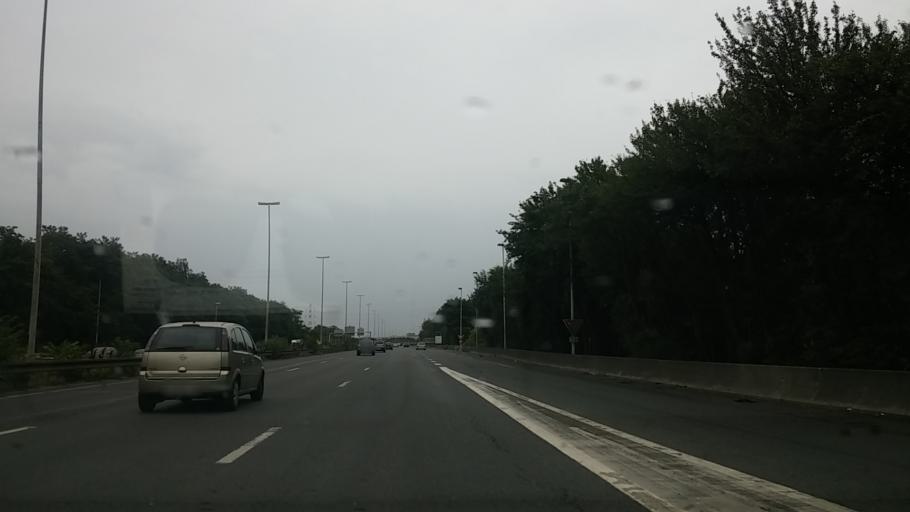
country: FR
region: Ile-de-France
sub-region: Departement de Seine-Saint-Denis
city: Villepinte
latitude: 48.9688
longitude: 2.5061
